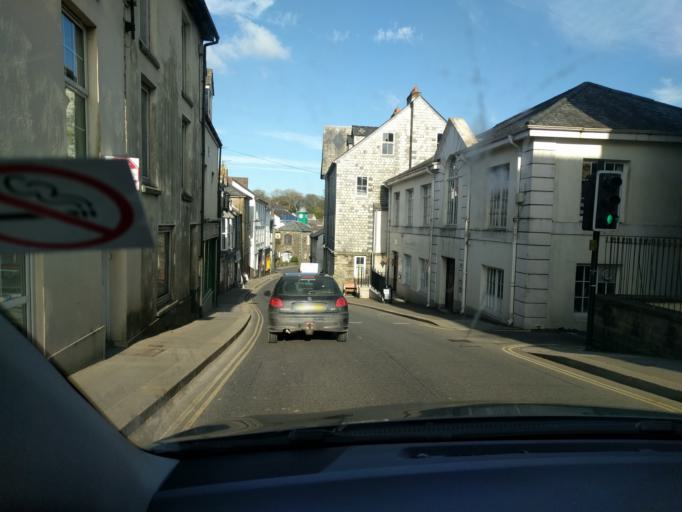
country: GB
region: England
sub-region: Cornwall
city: Camelford
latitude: 50.6214
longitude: -4.6796
